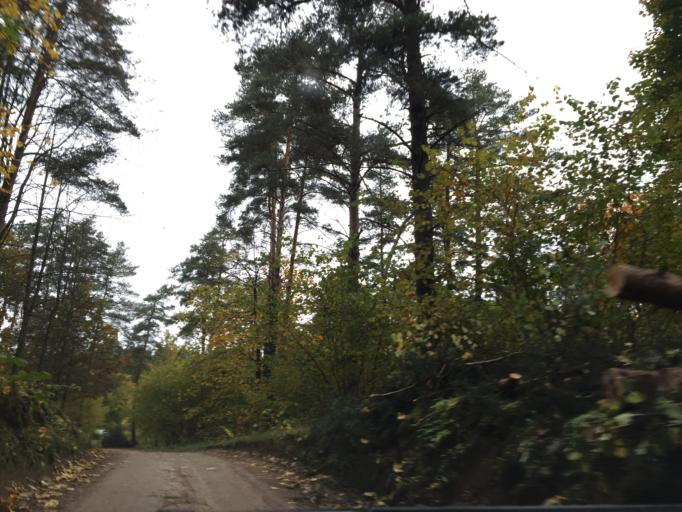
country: LV
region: Ogre
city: Ogre
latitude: 56.8034
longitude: 24.6364
